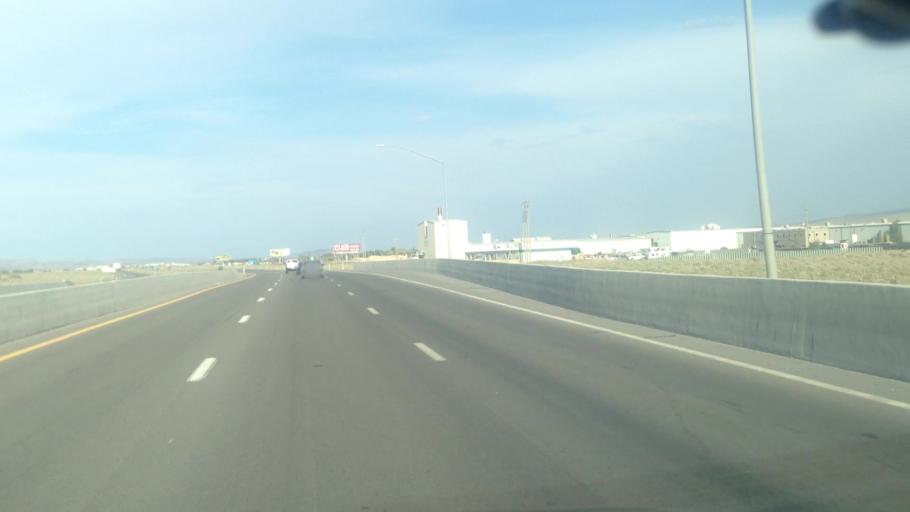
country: US
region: Nevada
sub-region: Lyon County
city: Fernley
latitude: 39.6155
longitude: -119.2620
